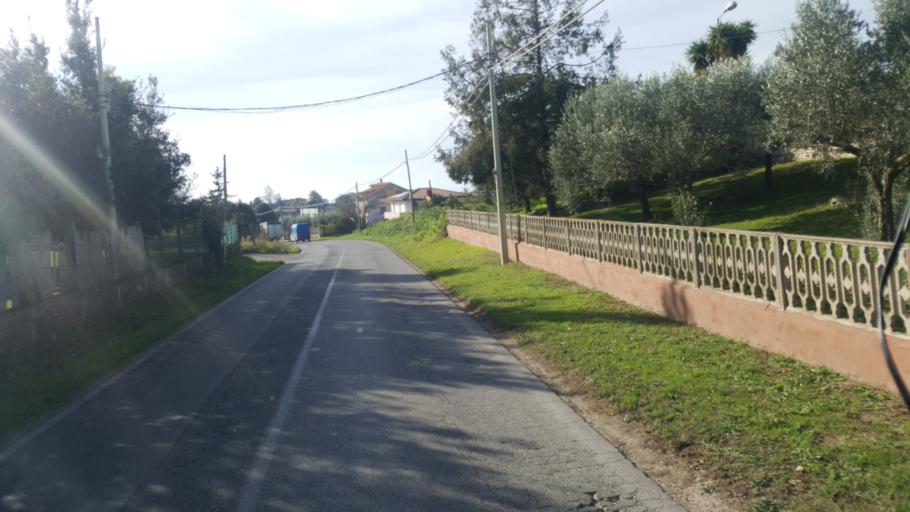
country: IT
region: Latium
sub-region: Provincia di Latina
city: Casalazzara
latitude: 41.6361
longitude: 12.6068
